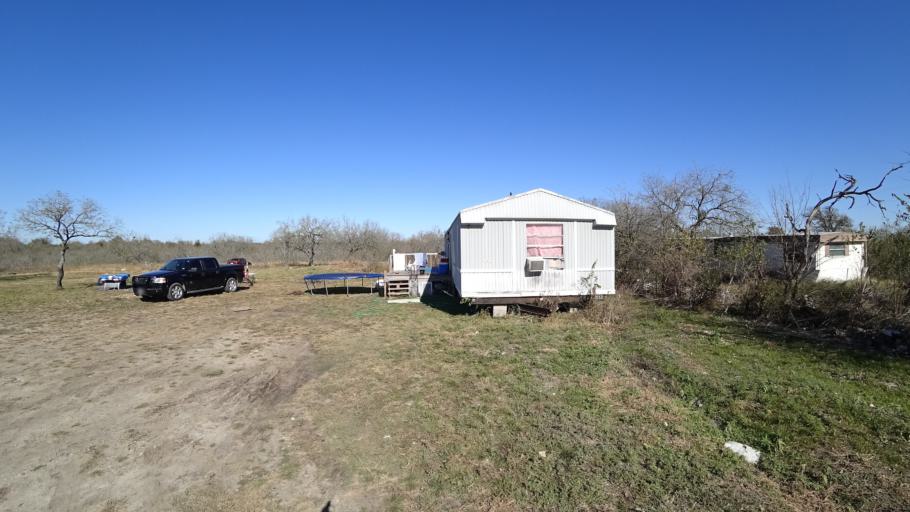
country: US
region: Texas
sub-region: Travis County
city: Garfield
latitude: 30.1296
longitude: -97.6071
